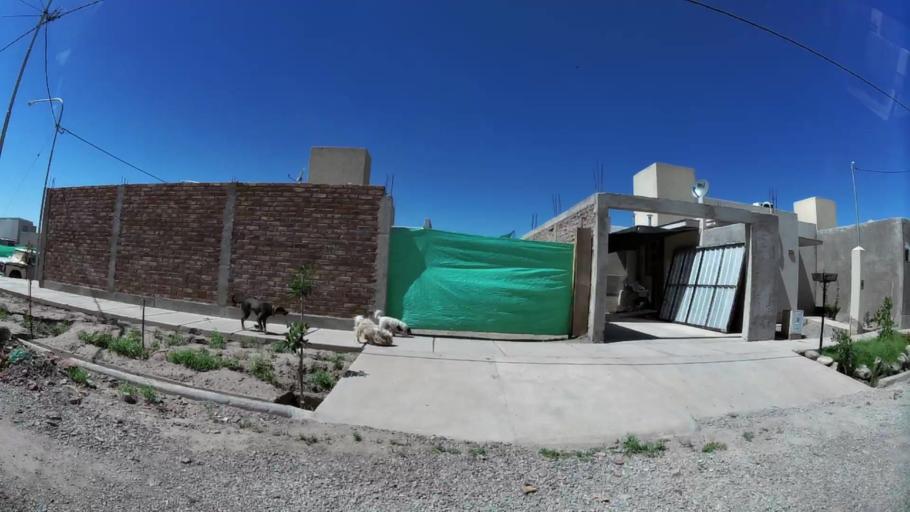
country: AR
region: Mendoza
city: Las Heras
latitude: -32.8495
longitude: -68.8569
